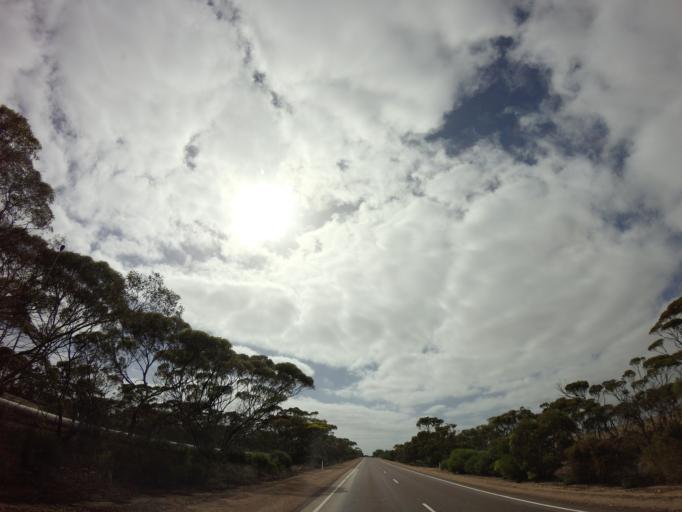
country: AU
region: South Australia
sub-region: Streaky Bay
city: Streaky Bay
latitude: -32.7302
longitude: 134.8751
